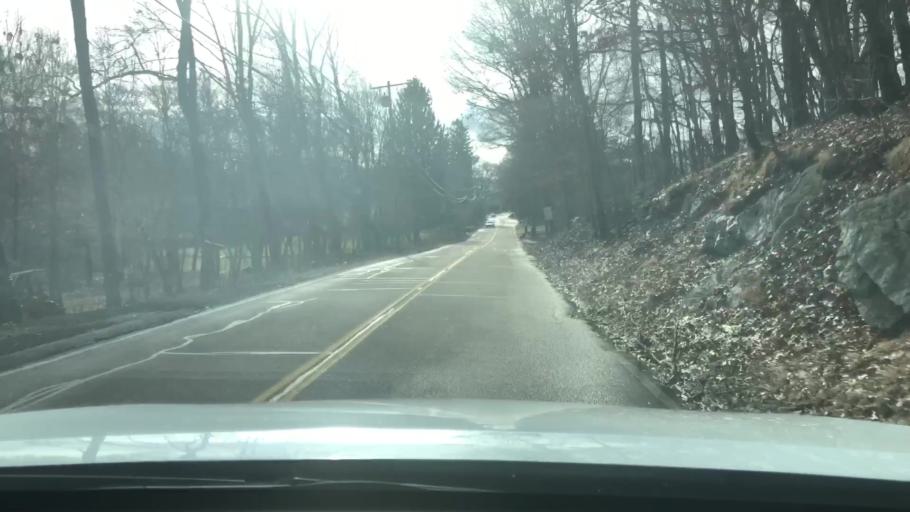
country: US
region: Massachusetts
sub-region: Worcester County
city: Blackstone
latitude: 42.0232
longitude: -71.5251
